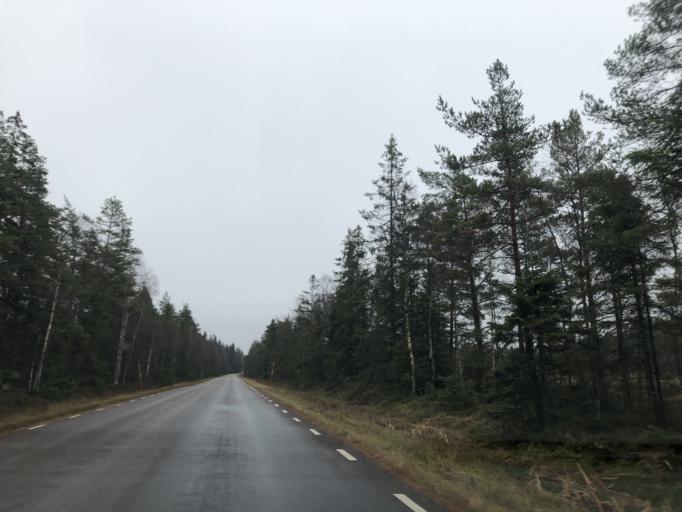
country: SE
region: Vaestra Goetaland
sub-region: Ulricehamns Kommun
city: Ulricehamn
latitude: 57.7567
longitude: 13.5025
